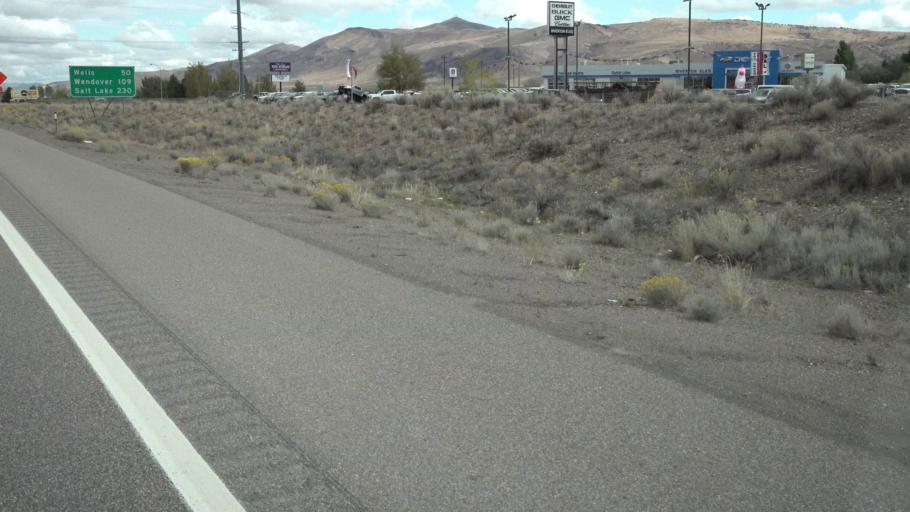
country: US
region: Nevada
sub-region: Elko County
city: Elko
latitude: 40.8607
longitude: -115.7379
